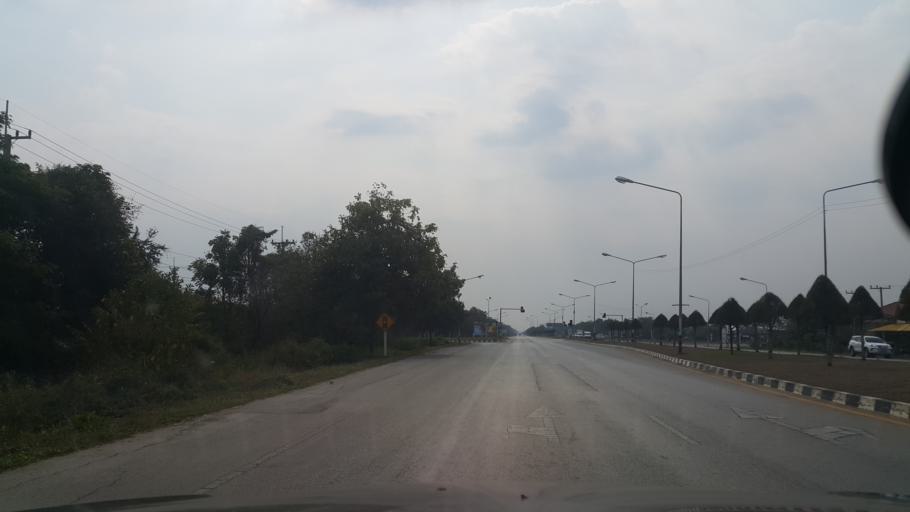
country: TH
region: Sukhothai
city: Sukhothai
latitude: 17.0535
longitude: 99.9015
